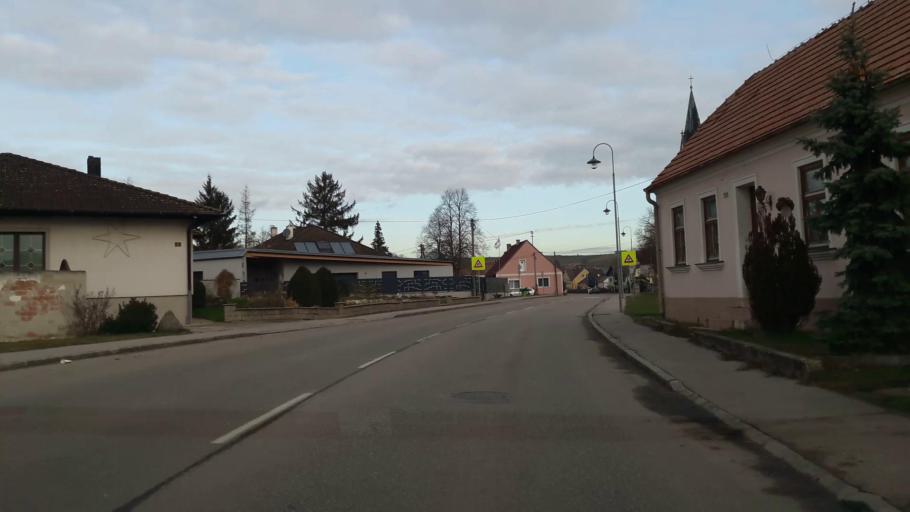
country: AT
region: Lower Austria
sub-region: Politischer Bezirk Mistelbach
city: Asparn an der Zaya
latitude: 48.6055
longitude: 16.5402
